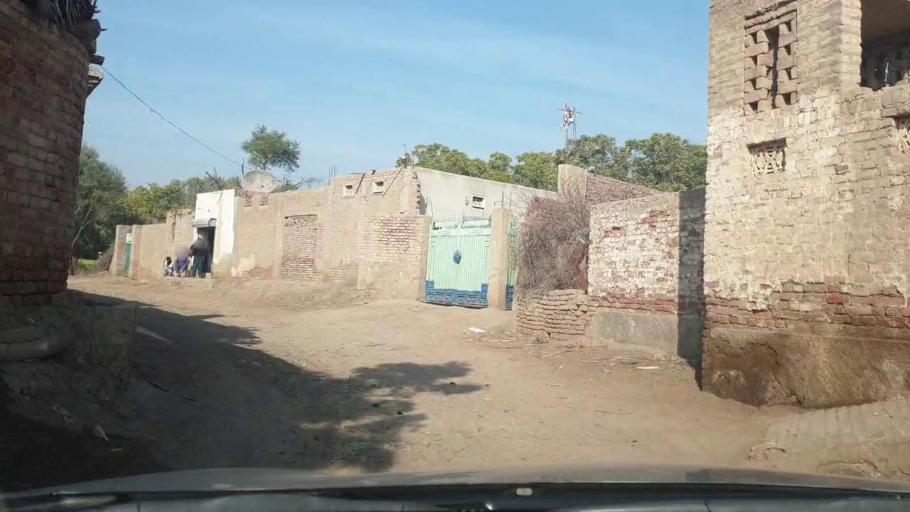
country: PK
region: Sindh
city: Tando Allahyar
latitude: 25.5941
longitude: 68.7213
